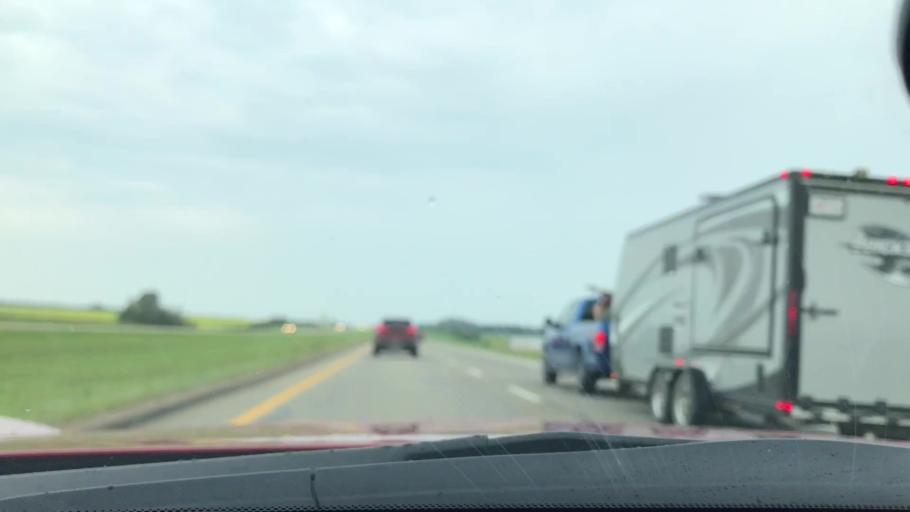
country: CA
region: Alberta
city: Millet
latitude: 53.0785
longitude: -113.5982
